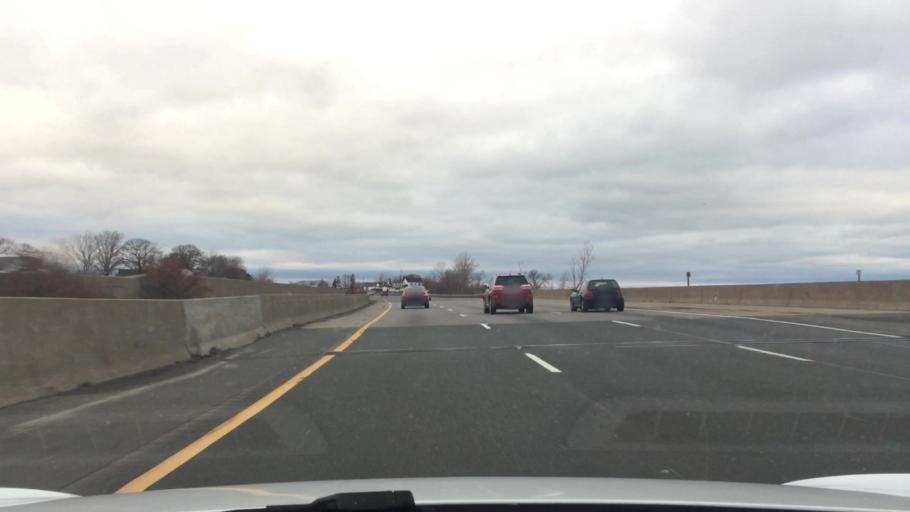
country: CA
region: Ontario
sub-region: Regional Municipality of Niagara
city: St. Catharines
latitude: 43.1847
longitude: -79.3728
